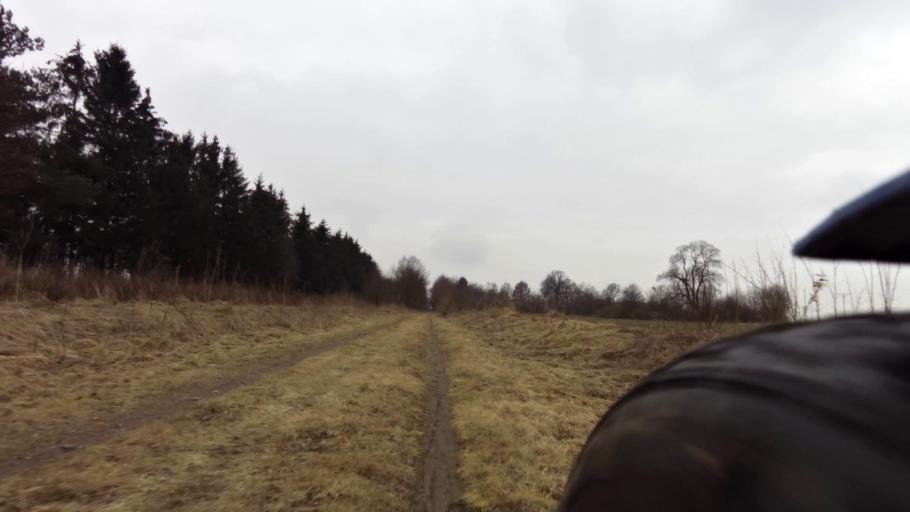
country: PL
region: West Pomeranian Voivodeship
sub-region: Powiat walecki
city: Walcz
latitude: 53.2504
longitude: 16.4768
